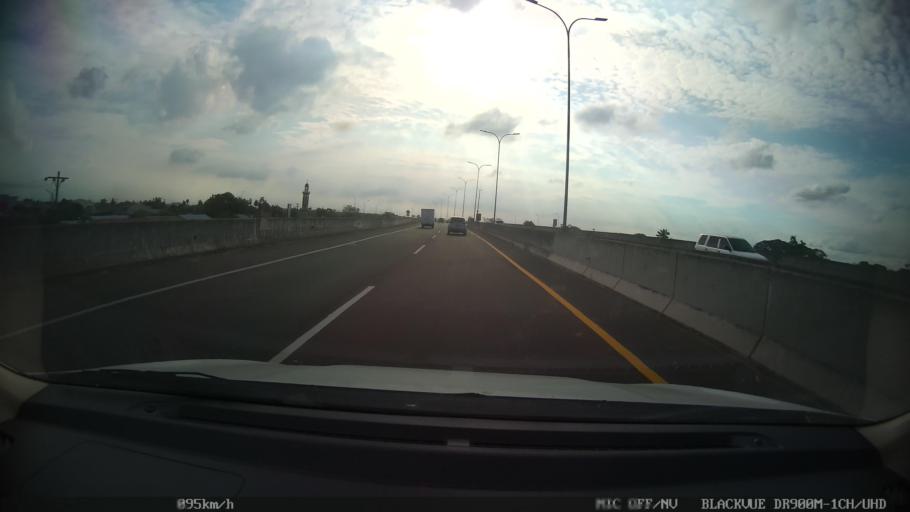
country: ID
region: North Sumatra
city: Medan
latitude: 3.6492
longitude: 98.6601
